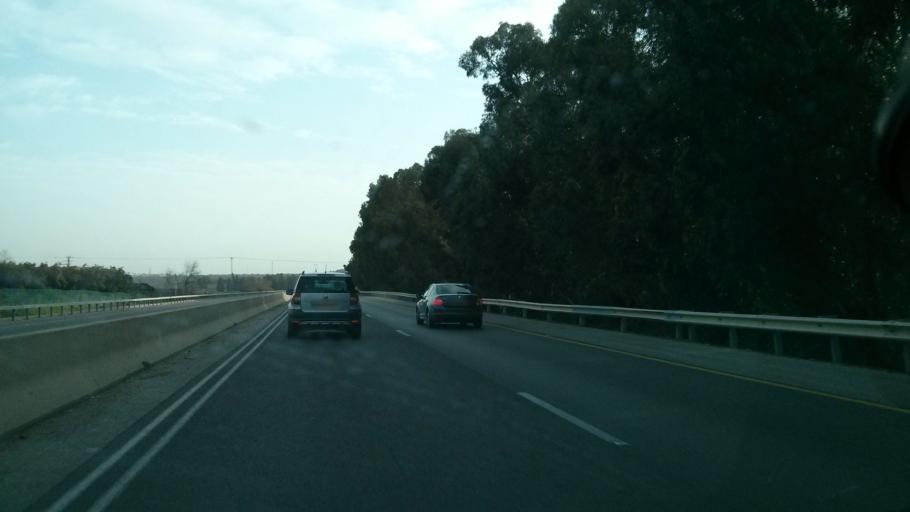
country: PS
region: West Bank
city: Nazlat `Isa
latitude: 32.4766
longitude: 35.0160
